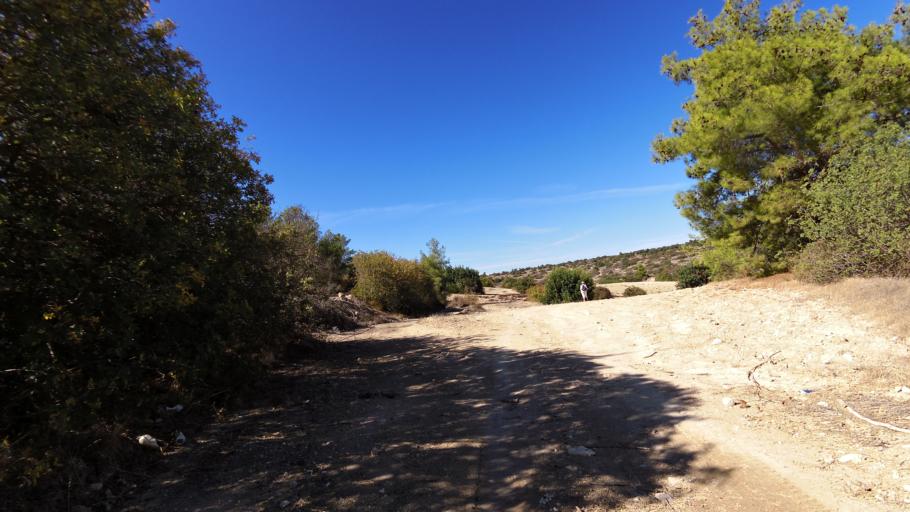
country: CY
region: Pafos
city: Polis
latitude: 35.0151
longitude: 32.4845
